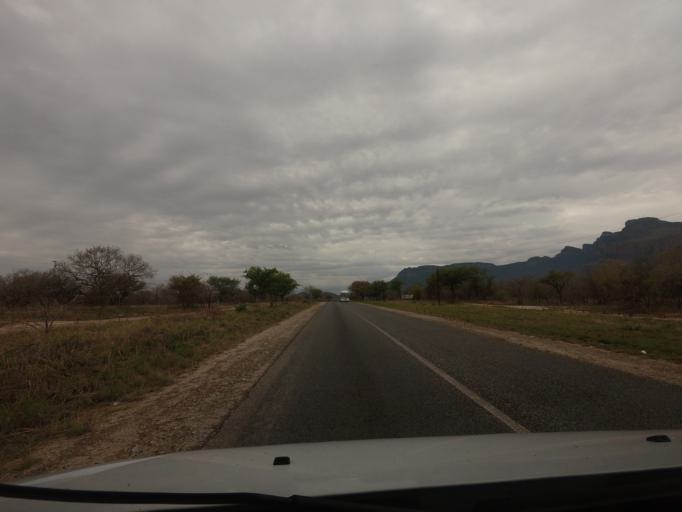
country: ZA
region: Limpopo
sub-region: Mopani District Municipality
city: Hoedspruit
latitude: -24.4804
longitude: 30.8856
